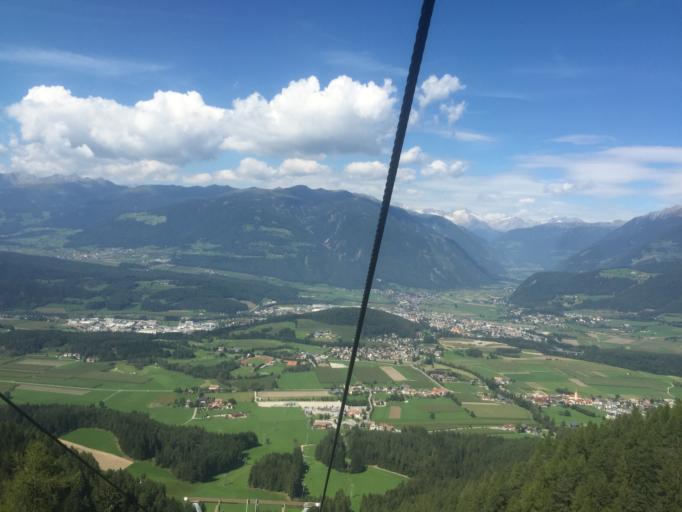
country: IT
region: Trentino-Alto Adige
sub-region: Bolzano
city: Riscone
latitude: 46.7585
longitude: 11.9475
